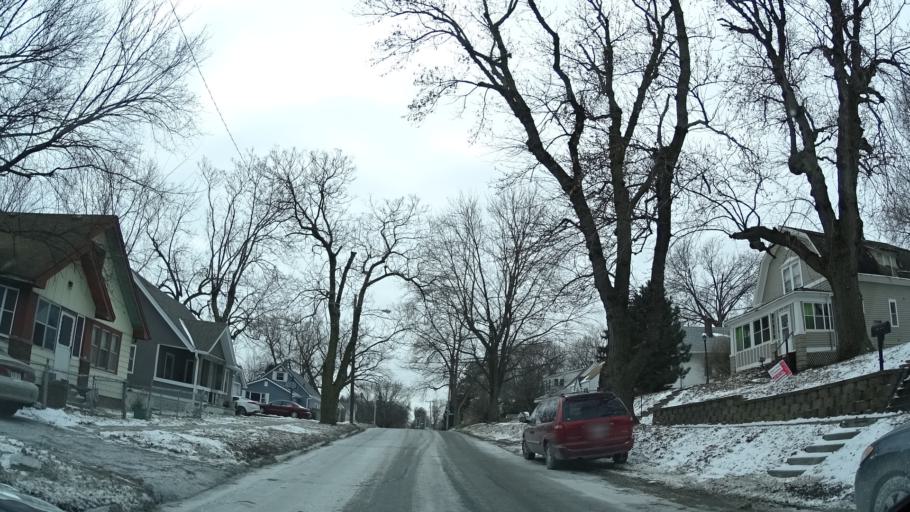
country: US
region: Nebraska
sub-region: Douglas County
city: Omaha
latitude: 41.2803
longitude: -96.0048
